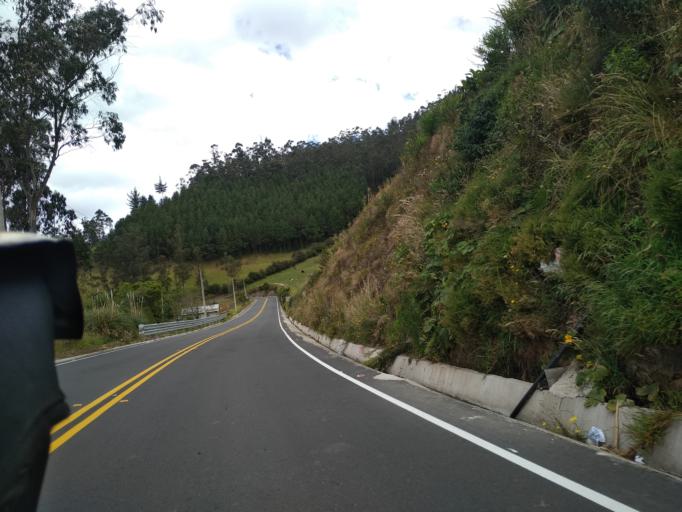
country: EC
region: Cotopaxi
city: Saquisili
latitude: -0.7149
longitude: -78.8854
